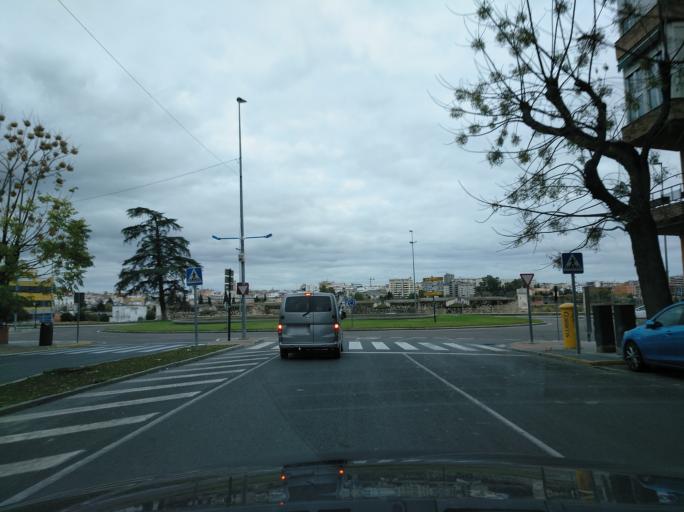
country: ES
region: Extremadura
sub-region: Provincia de Badajoz
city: Badajoz
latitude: 38.8858
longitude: -6.9802
